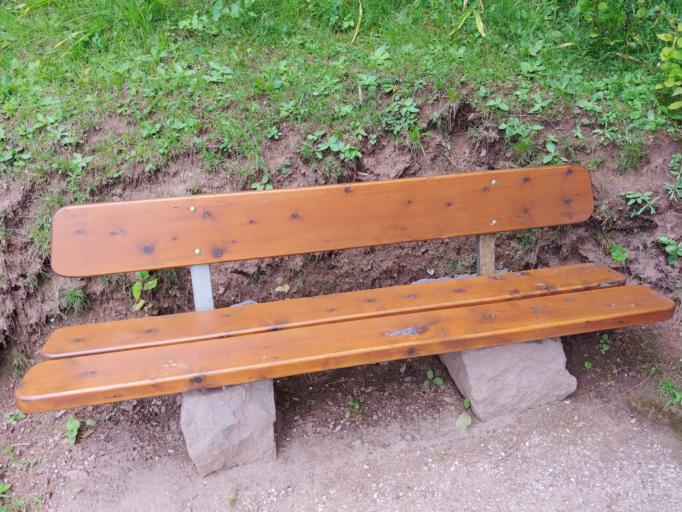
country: IT
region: Trentino-Alto Adige
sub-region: Bolzano
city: Ortisei
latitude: 46.5751
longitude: 11.6762
